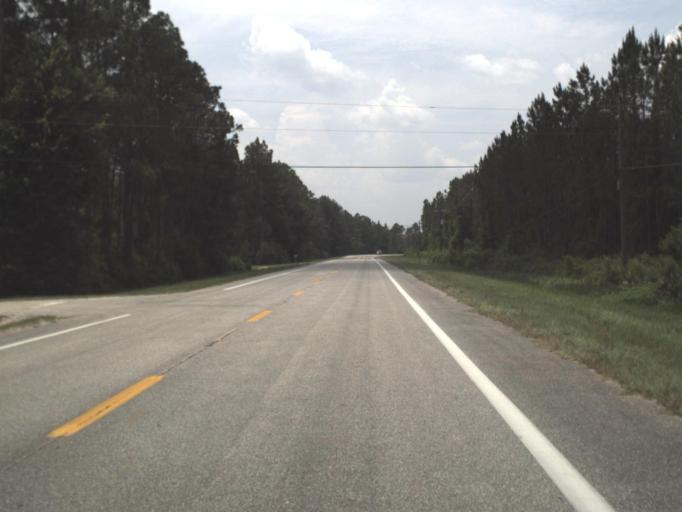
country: US
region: Florida
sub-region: Putnam County
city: Palatka
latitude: 29.5829
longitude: -81.7173
